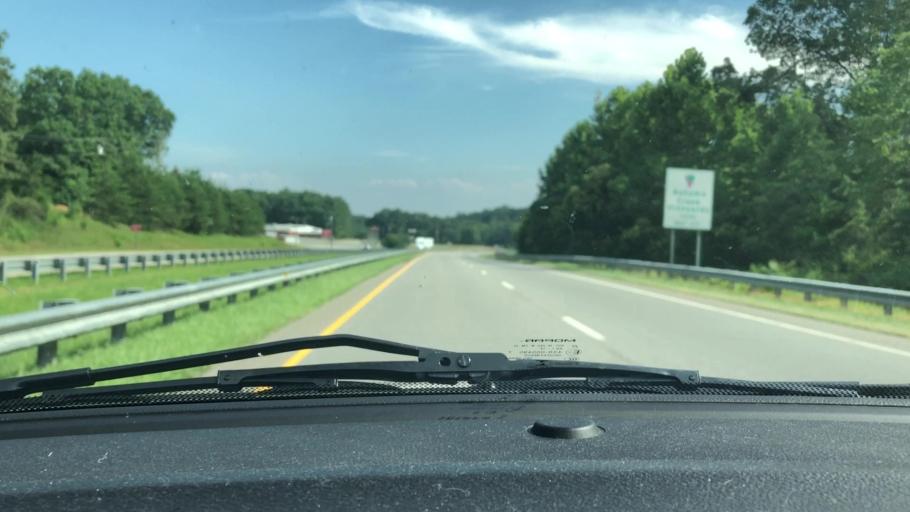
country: US
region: North Carolina
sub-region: Rockingham County
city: Stoneville
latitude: 36.4824
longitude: -79.9245
